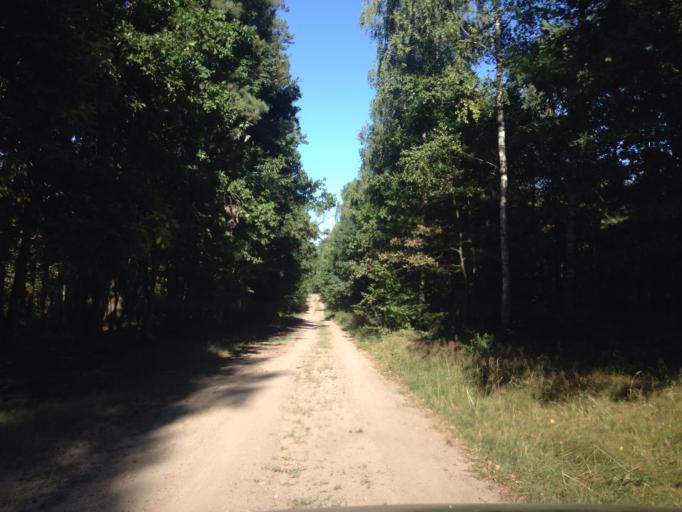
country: PL
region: Kujawsko-Pomorskie
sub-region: Powiat brodnicki
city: Gorzno
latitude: 53.1535
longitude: 19.6638
